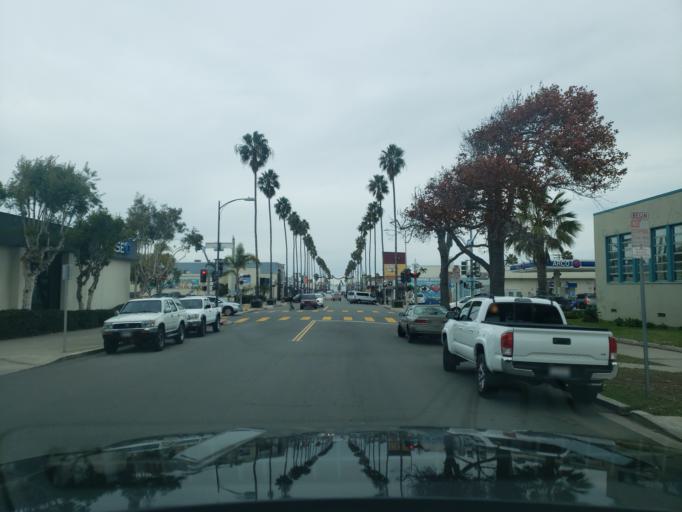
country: US
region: California
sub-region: San Diego County
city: Coronado
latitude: 32.7445
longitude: -117.2472
